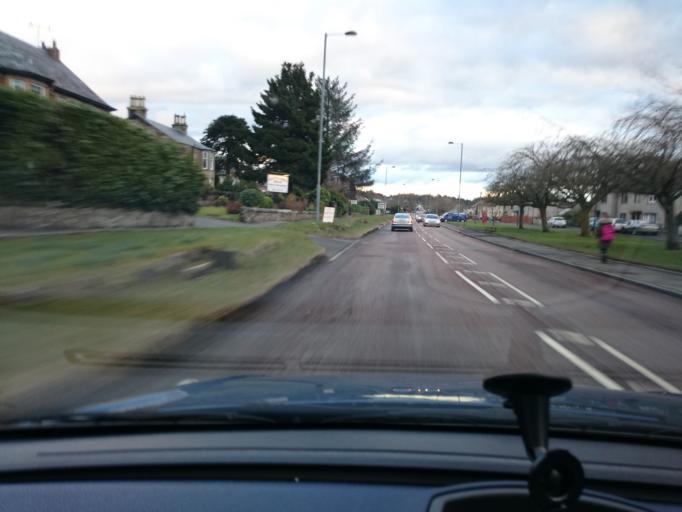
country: GB
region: Scotland
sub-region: Stirling
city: Callander
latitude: 56.2412
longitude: -4.2041
